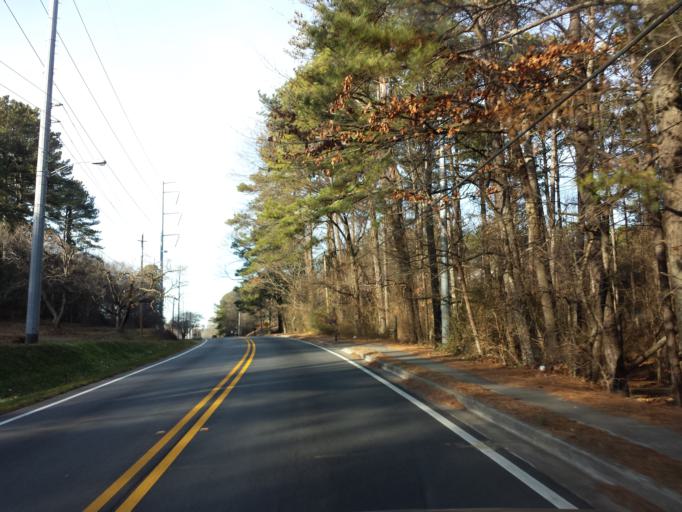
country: US
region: Georgia
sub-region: Cobb County
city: Marietta
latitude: 34.0047
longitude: -84.5455
